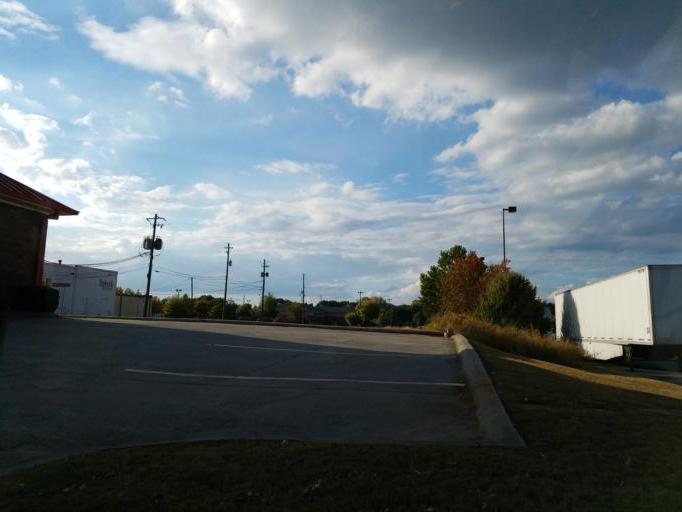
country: US
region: Georgia
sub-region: Bartow County
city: Cartersville
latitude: 34.1986
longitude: -84.7890
